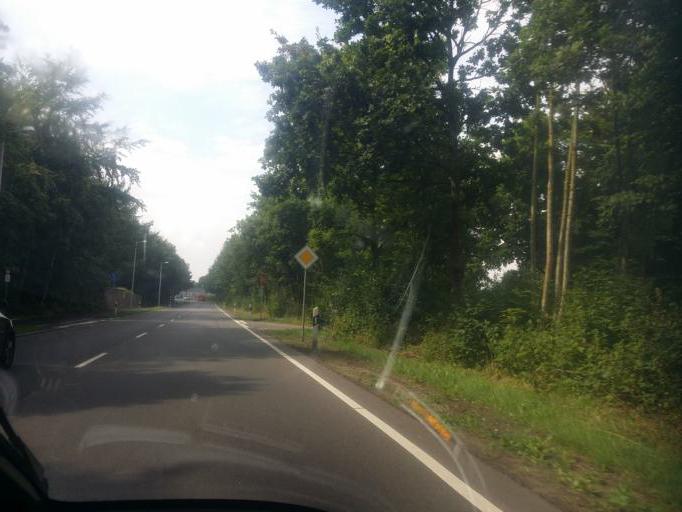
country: DE
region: Schleswig-Holstein
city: Heide
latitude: 54.2053
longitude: 9.1123
